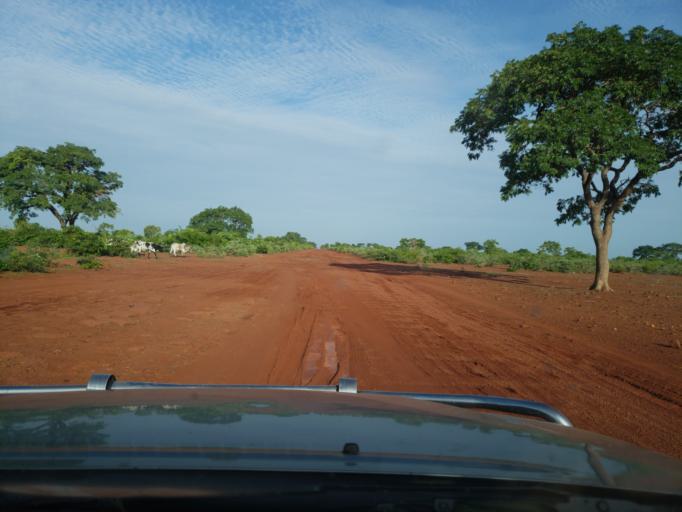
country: ML
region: Sikasso
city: Koutiala
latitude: 12.4284
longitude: -5.6246
